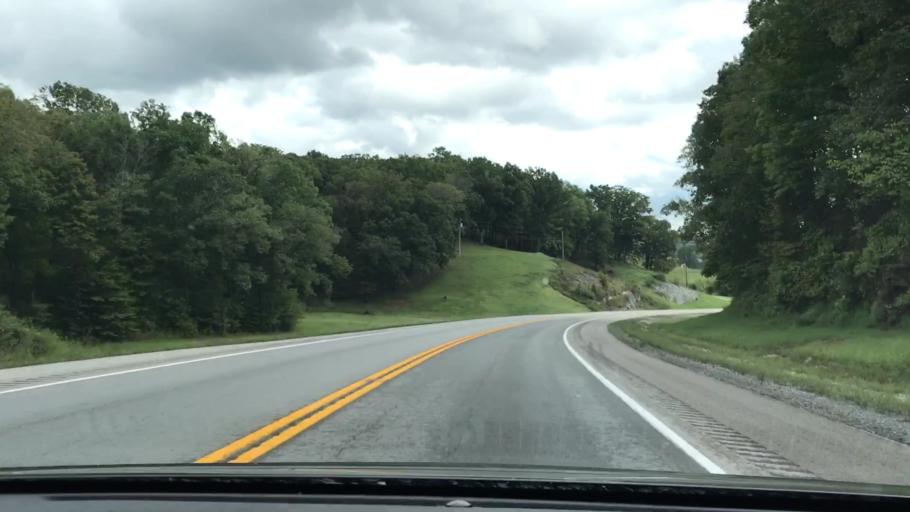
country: US
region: Kentucky
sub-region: Cumberland County
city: Burkesville
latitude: 36.8004
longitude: -85.3804
